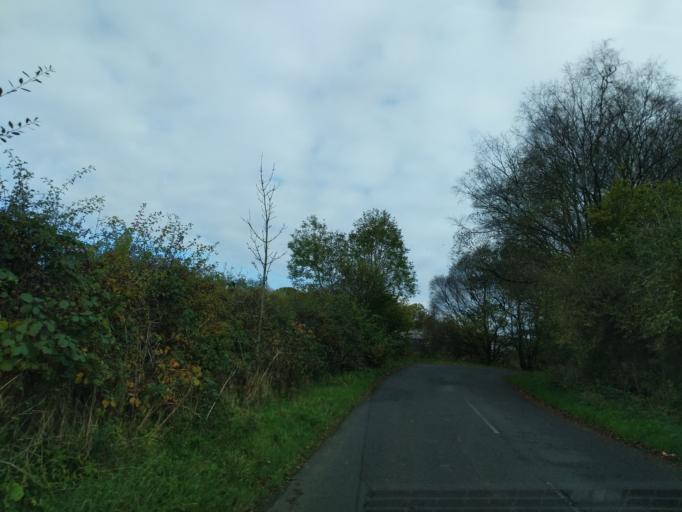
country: GB
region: Scotland
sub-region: Dumfries and Galloway
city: Castle Douglas
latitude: 55.1070
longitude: -4.1254
